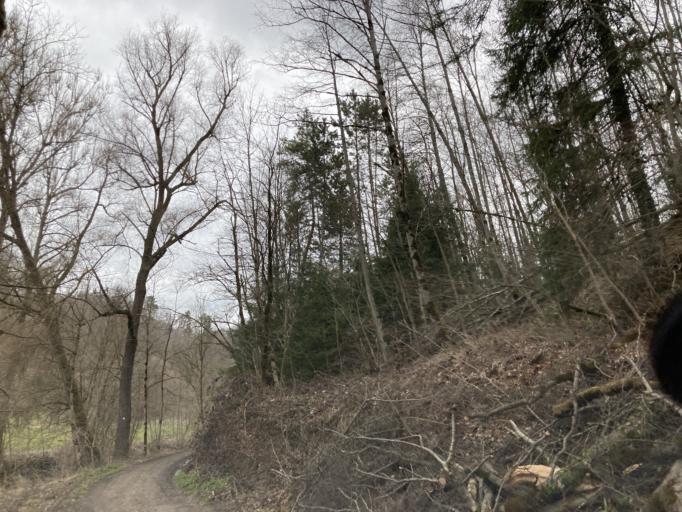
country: DE
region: Baden-Wuerttemberg
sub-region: Tuebingen Region
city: Hirrlingen
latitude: 48.4227
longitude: 8.8663
